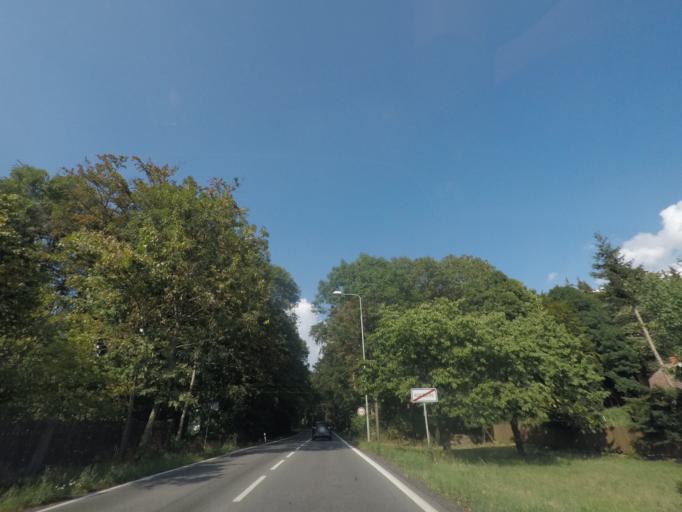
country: CZ
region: Kralovehradecky
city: Dvur Kralove nad Labem
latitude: 50.4630
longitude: 15.8634
